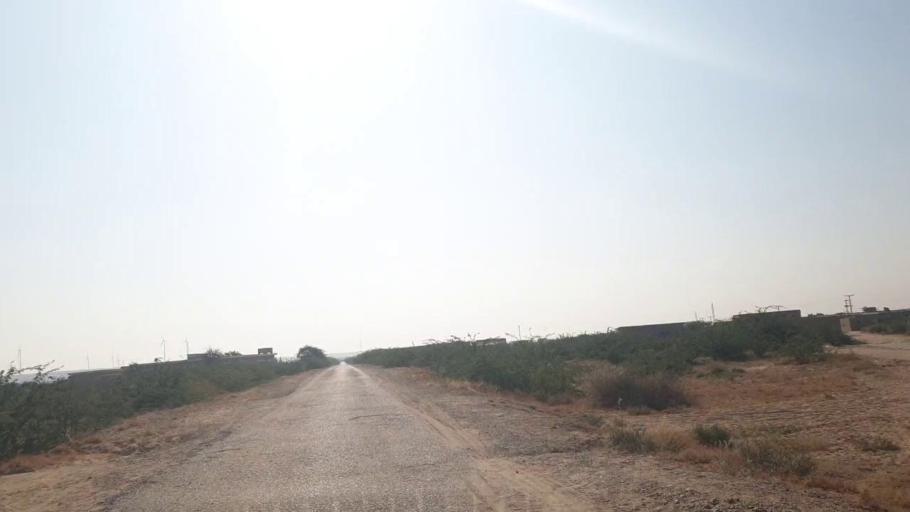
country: PK
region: Sindh
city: Thatta
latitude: 25.1352
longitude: 67.7723
